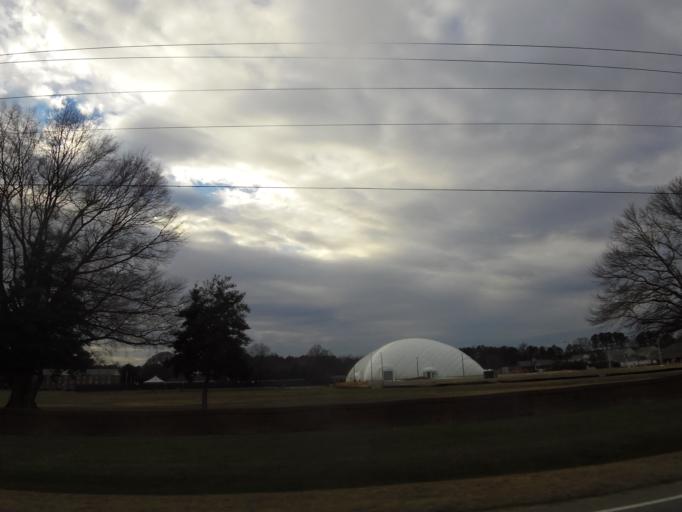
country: US
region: North Carolina
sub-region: Nash County
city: Rocky Mount
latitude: 36.0215
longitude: -77.7697
